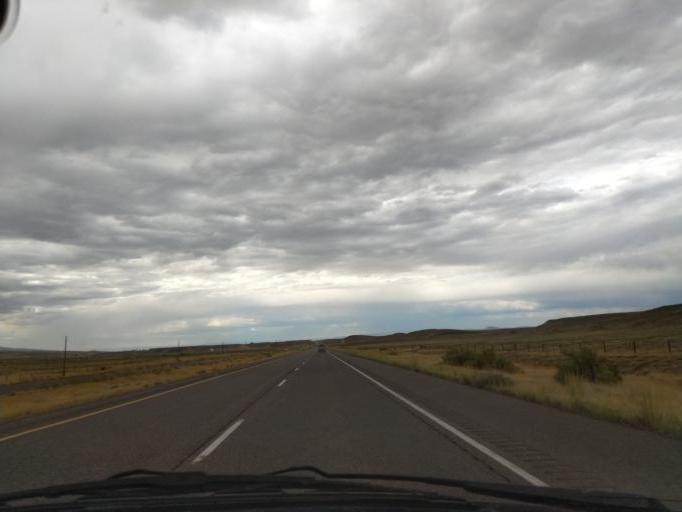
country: US
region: Colorado
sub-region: Mesa County
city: Clifton
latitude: 38.8989
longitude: -108.3658
